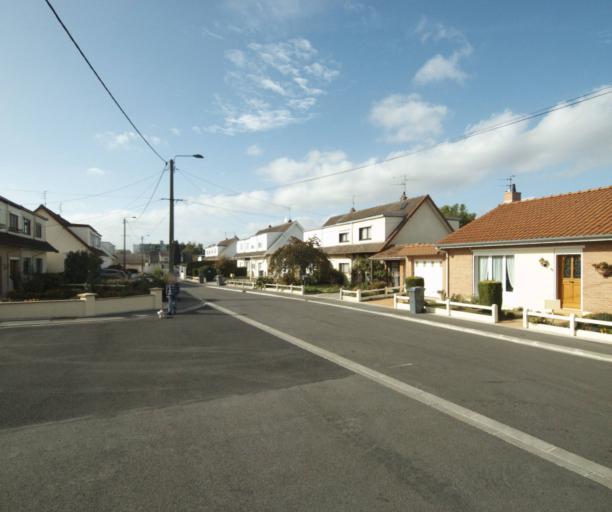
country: FR
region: Nord-Pas-de-Calais
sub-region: Departement du Nord
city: La Bassee
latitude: 50.5393
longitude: 2.8104
